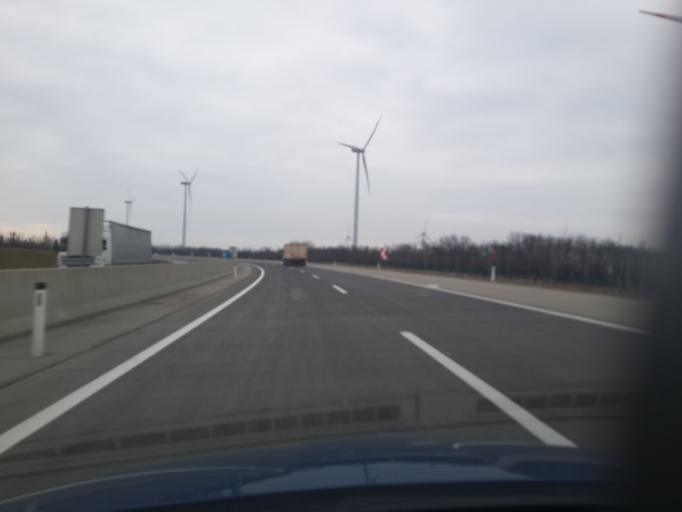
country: AT
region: Burgenland
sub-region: Politischer Bezirk Neusiedl am See
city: Potzneusiedl
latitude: 48.0400
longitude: 16.9002
